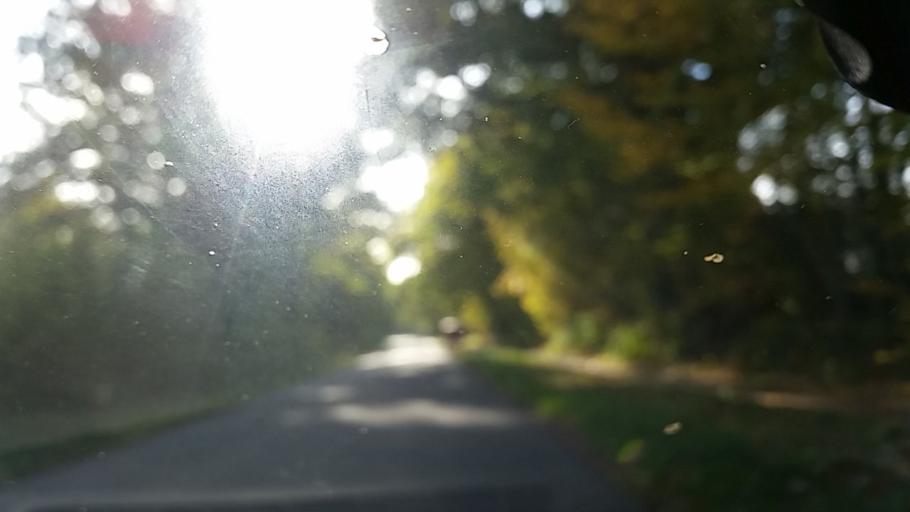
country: DE
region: Hamburg
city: Wohldorf-Ohlstedt
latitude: 53.7129
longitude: 10.1348
